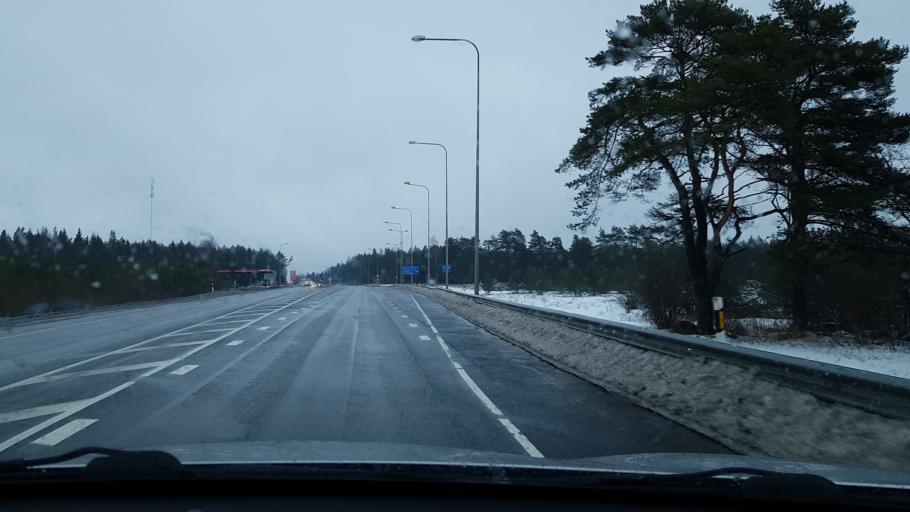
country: EE
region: Raplamaa
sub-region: Kohila vald
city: Kohila
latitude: 59.1795
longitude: 24.7799
